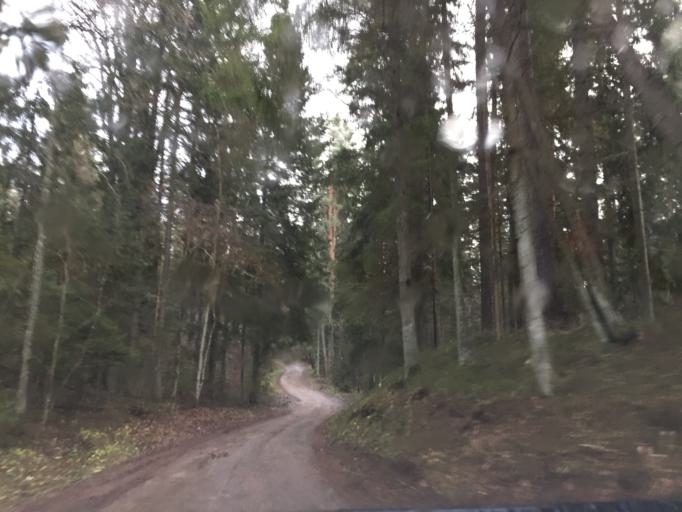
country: LV
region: Valmieras Rajons
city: Valmiera
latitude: 57.5505
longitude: 25.4760
